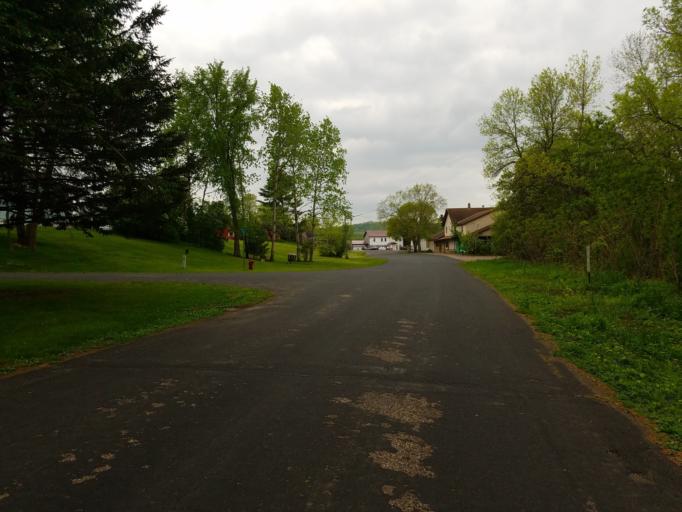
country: US
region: Wisconsin
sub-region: Dunn County
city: Menomonie
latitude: 44.7761
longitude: -91.9316
